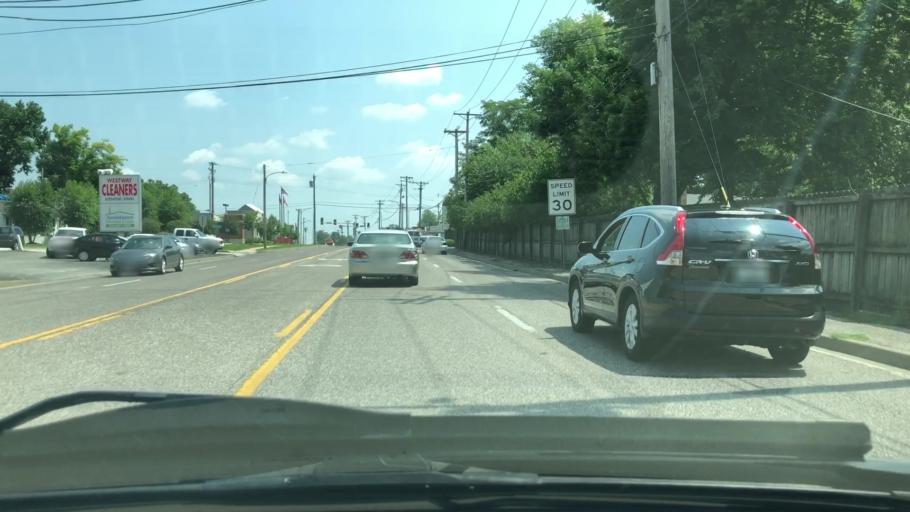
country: US
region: Missouri
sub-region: Saint Louis County
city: Rock Hill
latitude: 38.6044
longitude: -90.3801
